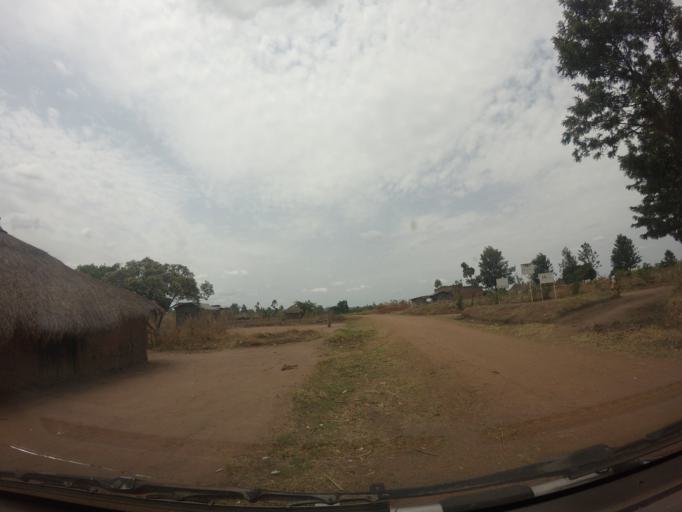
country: UG
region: Northern Region
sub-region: Arua District
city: Arua
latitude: 2.8215
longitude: 30.9022
